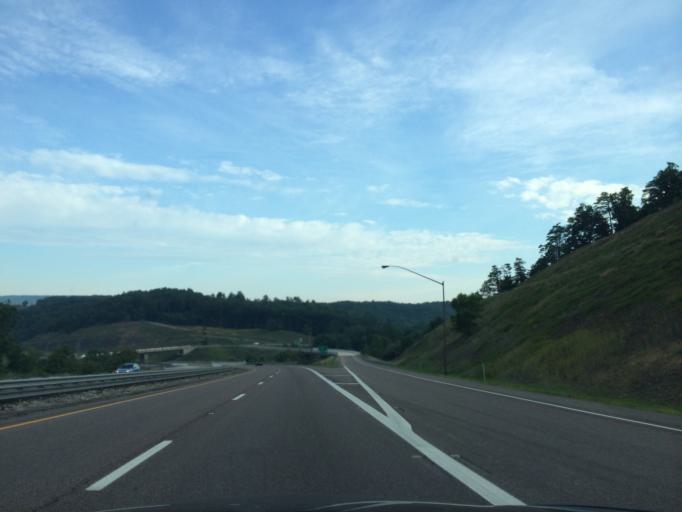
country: US
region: West Virginia
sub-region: Morgan County
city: Berkeley Springs
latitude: 39.6732
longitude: -78.4559
